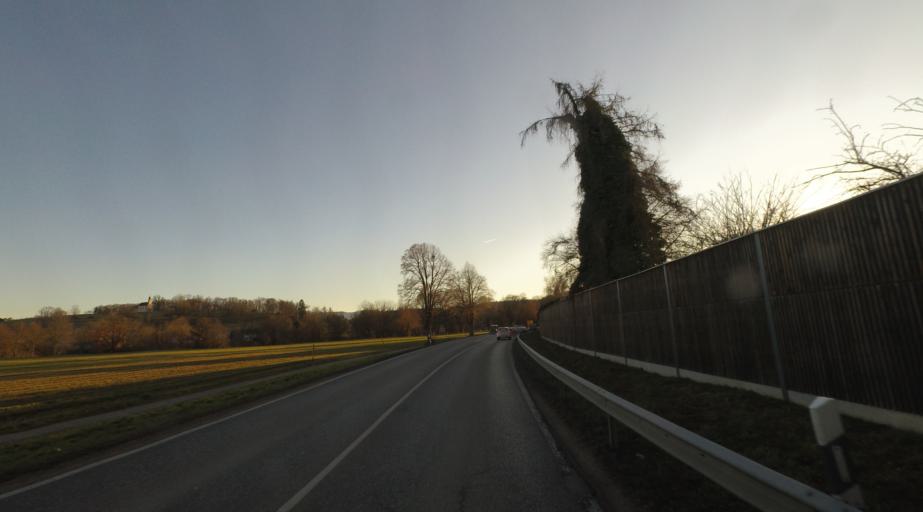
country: DE
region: Bavaria
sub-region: Upper Bavaria
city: Waging am See
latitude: 47.9365
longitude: 12.7442
